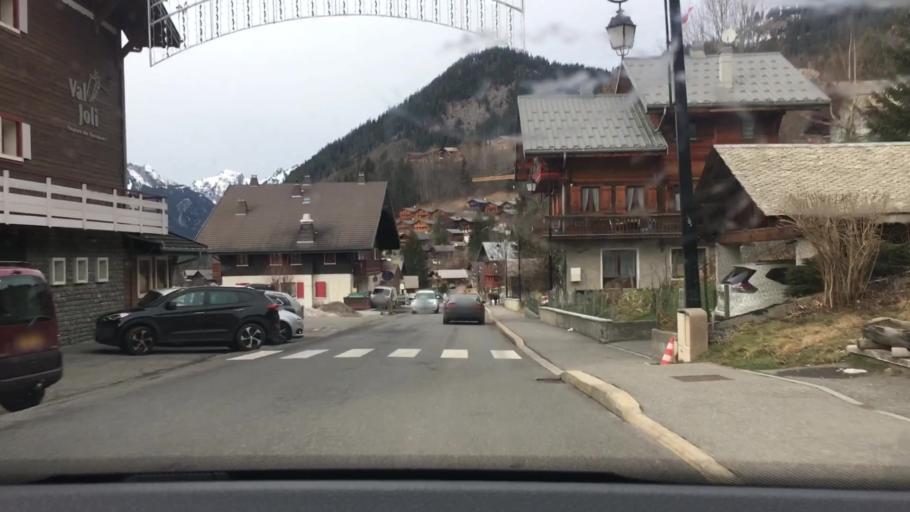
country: FR
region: Rhone-Alpes
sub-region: Departement de la Haute-Savoie
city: Chatel
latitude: 46.2727
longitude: 6.8382
